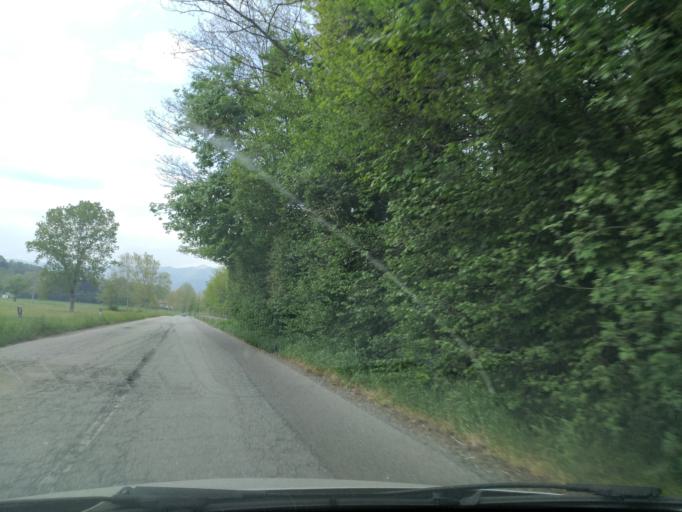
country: IT
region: Lombardy
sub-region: Provincia di Como
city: Brenna
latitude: 45.7553
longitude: 9.1807
